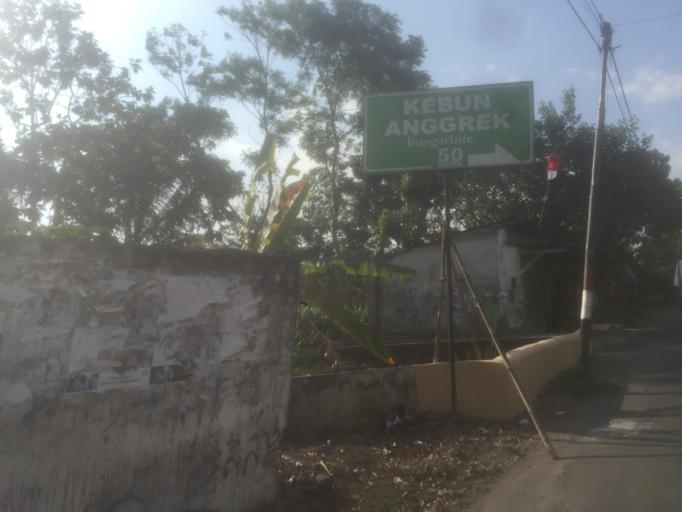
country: ID
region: Daerah Istimewa Yogyakarta
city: Sleman
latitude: -7.6750
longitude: 110.4173
